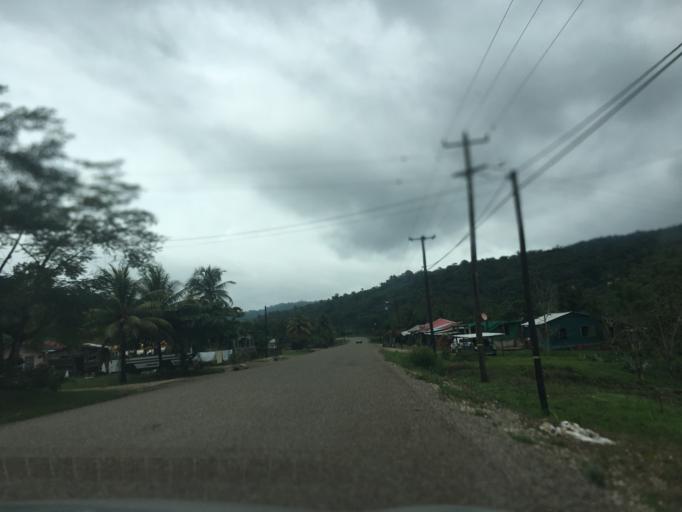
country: BZ
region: Stann Creek
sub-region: Dangriga
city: Dangriga
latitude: 17.0443
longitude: -88.5303
